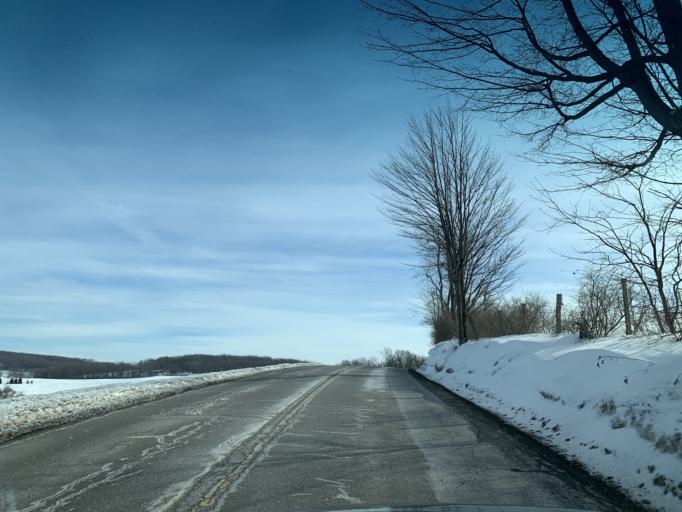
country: US
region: Maryland
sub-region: Allegany County
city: Frostburg
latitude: 39.6673
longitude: -78.8901
